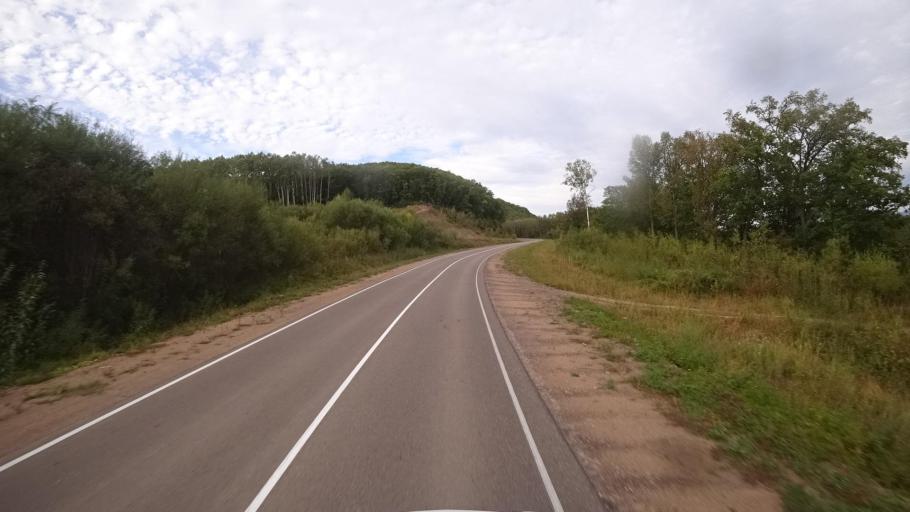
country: RU
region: Primorskiy
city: Yakovlevka
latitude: 44.3846
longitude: 133.4585
